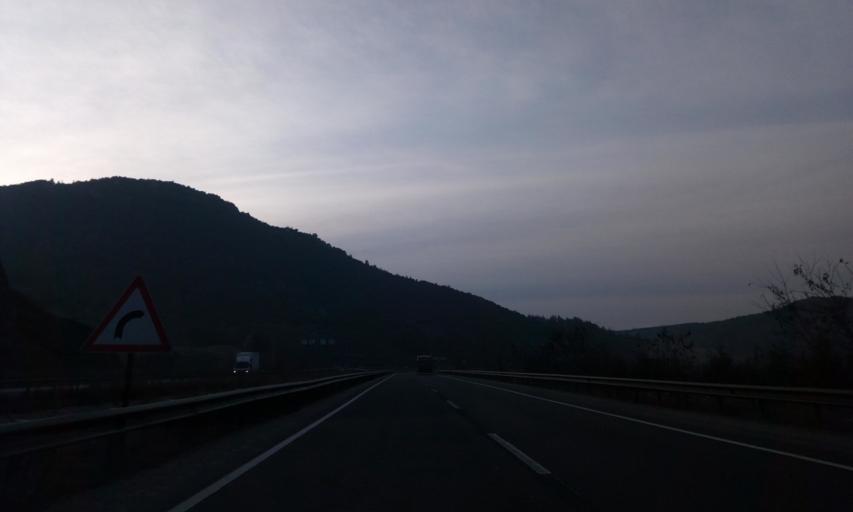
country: TR
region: Bilecik
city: Bilecik
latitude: 40.1668
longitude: 30.0199
